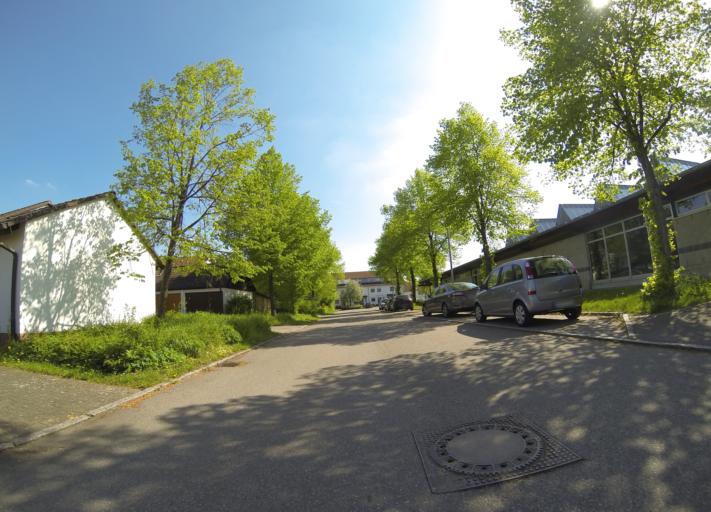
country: DE
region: Baden-Wuerttemberg
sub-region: Tuebingen Region
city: Ulm
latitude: 48.3533
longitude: 9.9770
